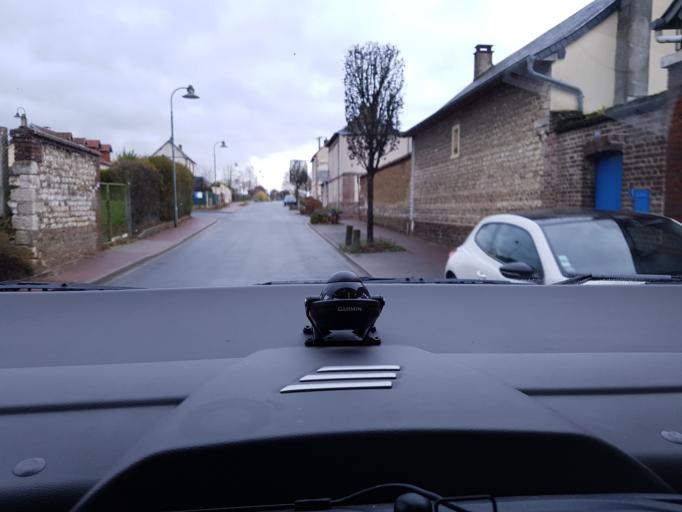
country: FR
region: Haute-Normandie
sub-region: Departement de l'Eure
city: Alizay
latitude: 49.3213
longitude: 1.1842
